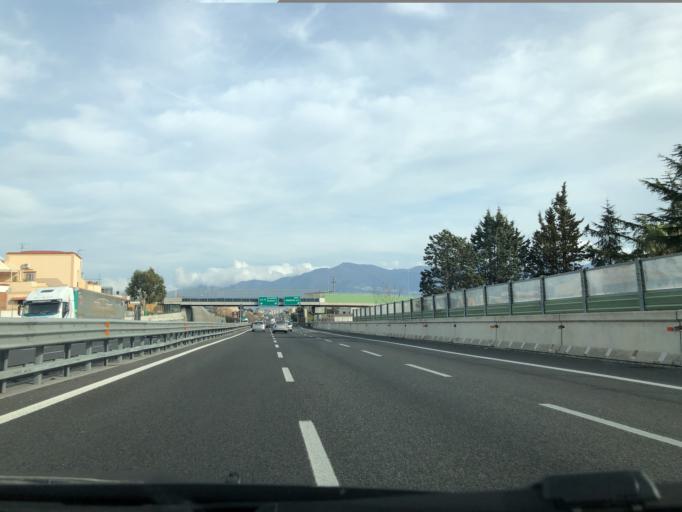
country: IT
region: Campania
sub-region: Provincia di Napoli
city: Trecase
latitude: 40.7681
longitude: 14.4248
